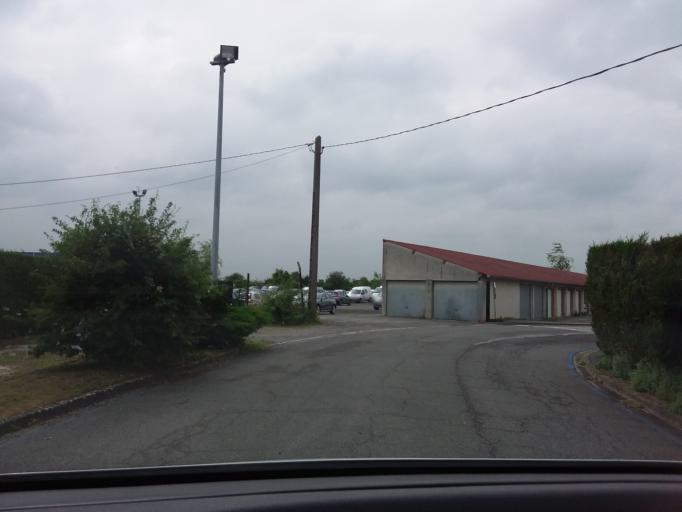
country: FR
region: Picardie
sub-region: Departement de l'Aisne
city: Laon
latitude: 49.5848
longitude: 3.6434
